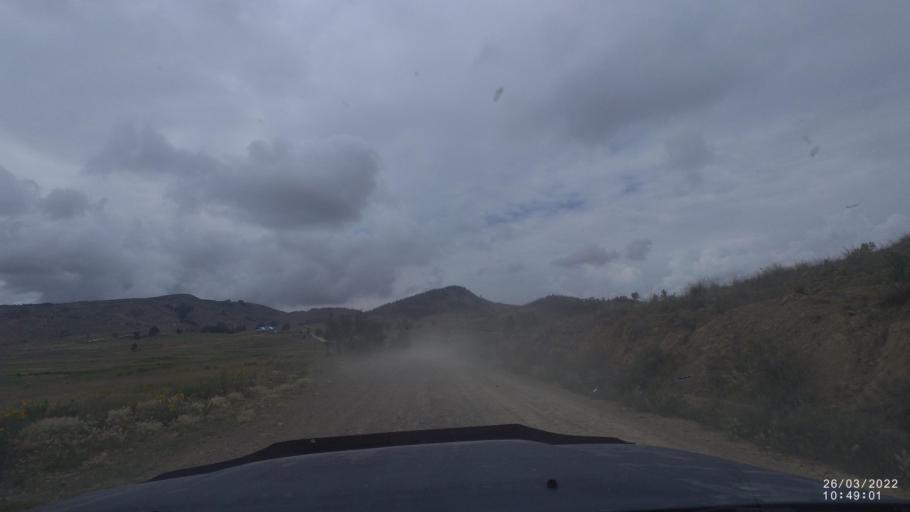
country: BO
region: Cochabamba
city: Tarata
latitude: -17.4999
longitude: -66.0412
